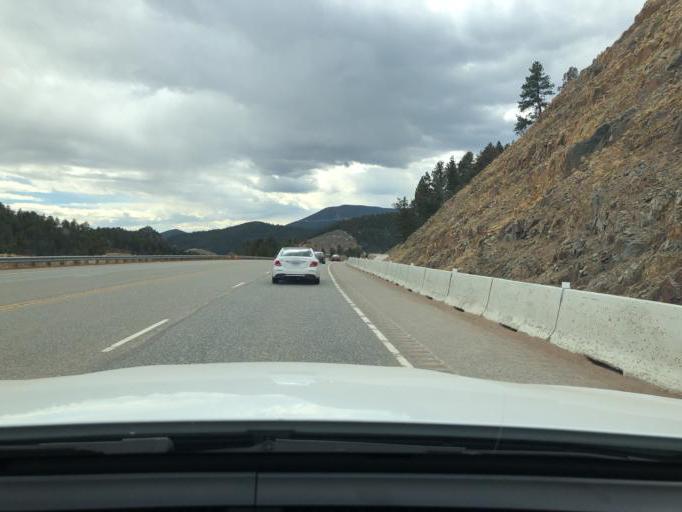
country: US
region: Colorado
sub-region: Gilpin County
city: Central City
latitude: 39.7765
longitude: -105.4746
